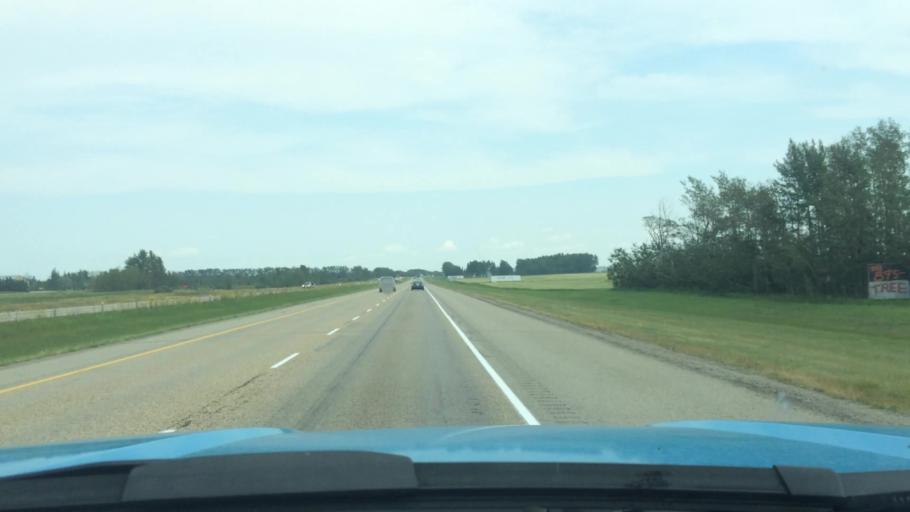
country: CA
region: Alberta
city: Penhold
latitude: 51.9701
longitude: -114.0026
